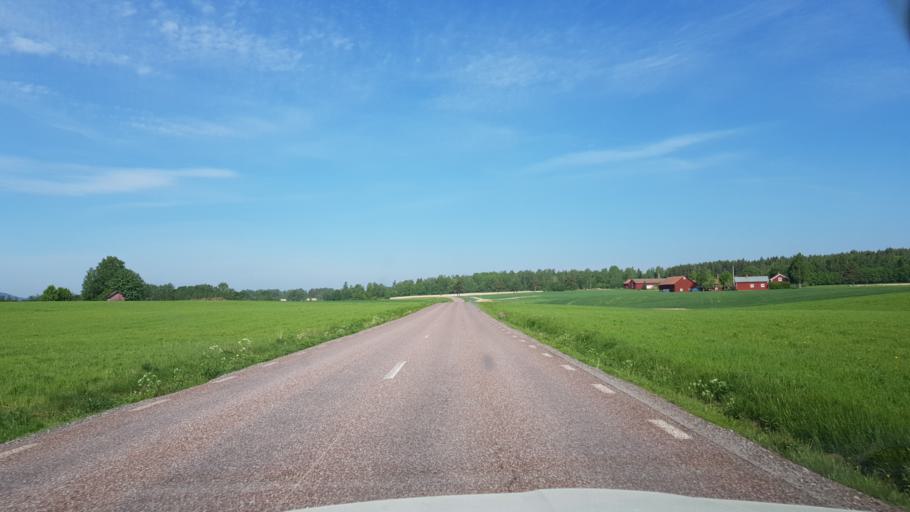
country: SE
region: Dalarna
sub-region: Saters Kommun
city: Saeter
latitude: 60.4240
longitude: 15.6492
